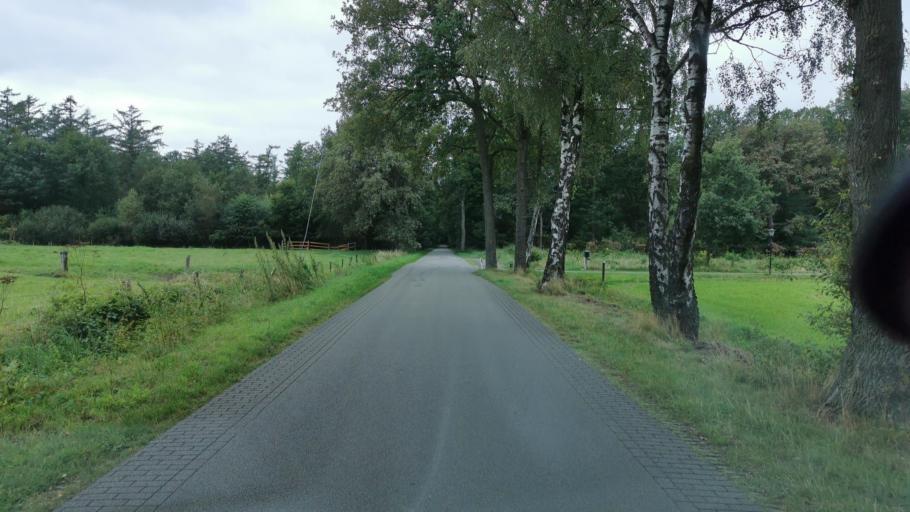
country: NL
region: Overijssel
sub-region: Gemeente Enschede
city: Enschede
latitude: 52.2318
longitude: 6.9489
